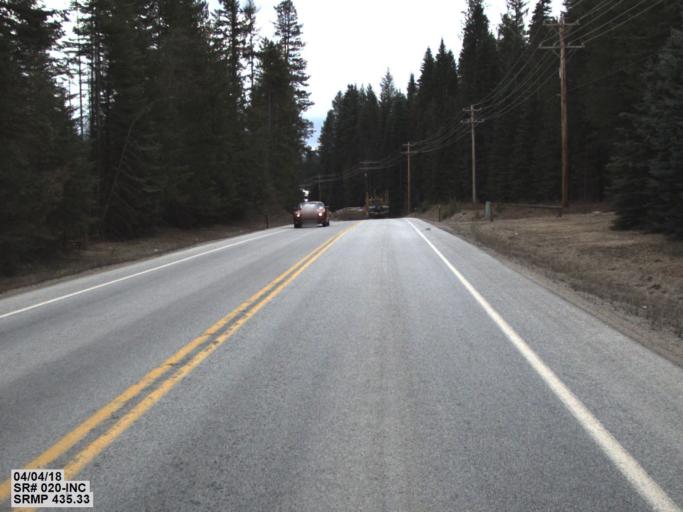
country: US
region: Washington
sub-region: Pend Oreille County
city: Newport
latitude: 48.2019
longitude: -117.0629
